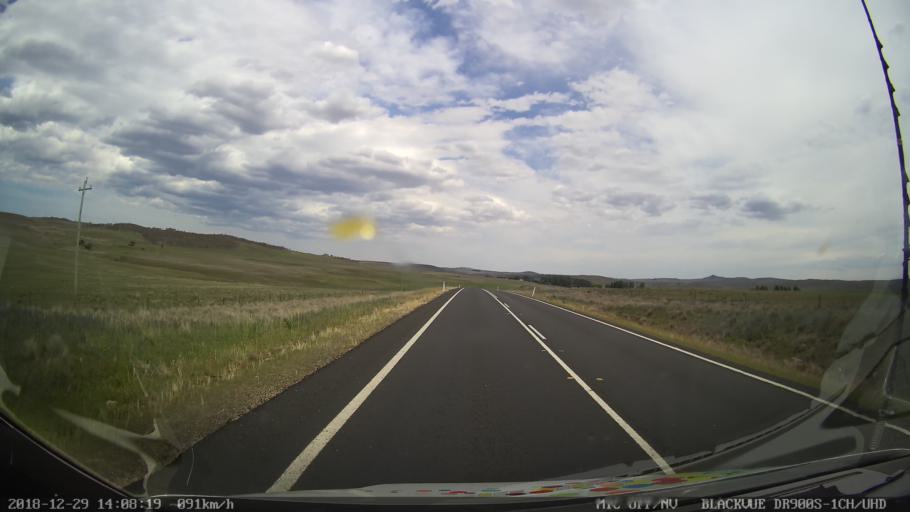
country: AU
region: New South Wales
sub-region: Cooma-Monaro
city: Cooma
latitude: -36.3637
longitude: 149.2143
